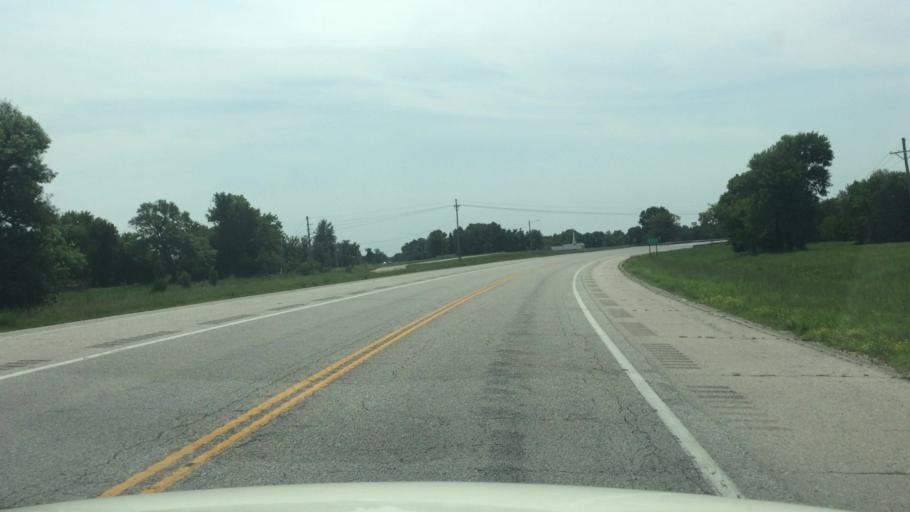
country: US
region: Kansas
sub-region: Cherokee County
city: Galena
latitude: 37.0874
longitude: -94.7044
